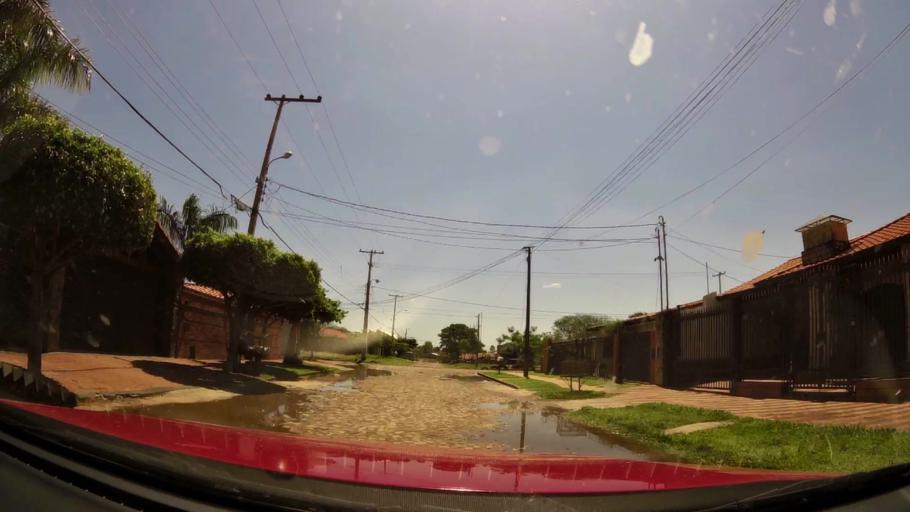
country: PY
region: Central
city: Colonia Mariano Roque Alonso
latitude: -25.2319
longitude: -57.5483
